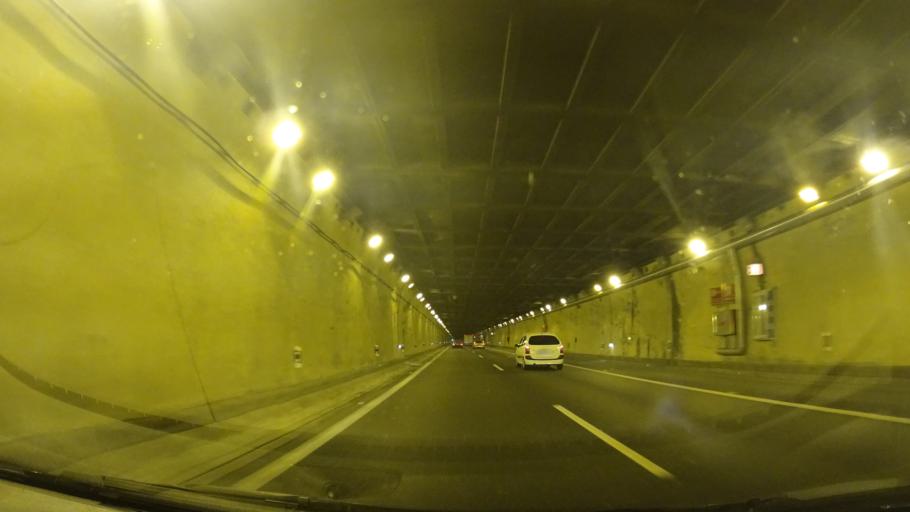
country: ES
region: Madrid
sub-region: Provincia de Madrid
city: Guadarrama
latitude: 40.7021
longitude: -4.1310
